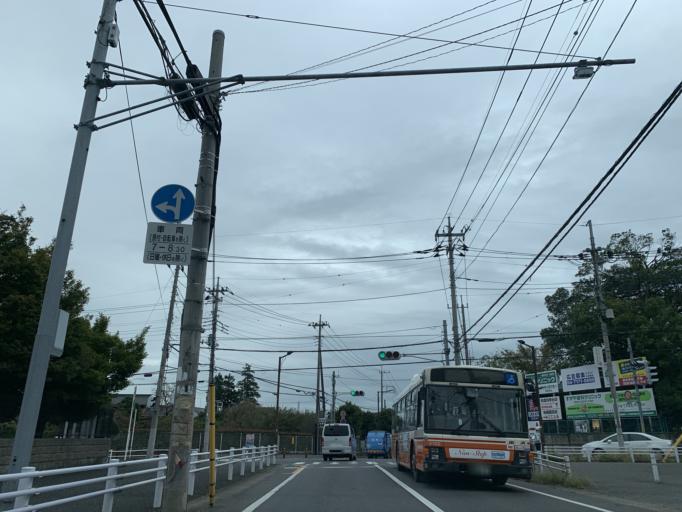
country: JP
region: Chiba
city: Kashiwa
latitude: 35.8715
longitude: 139.9503
